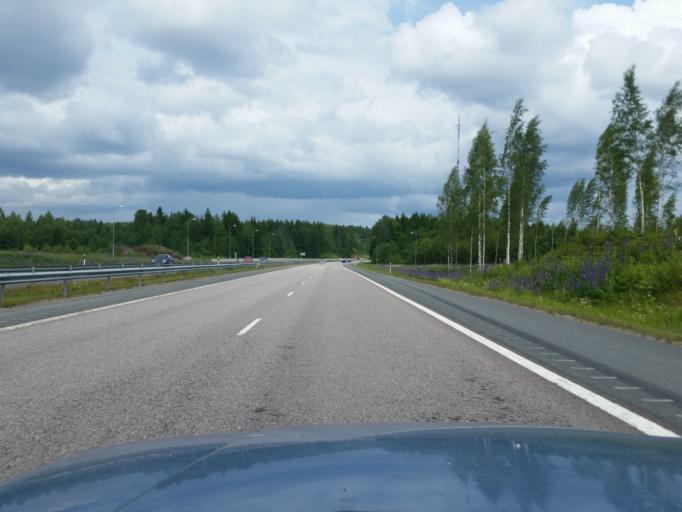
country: FI
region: Paijanne Tavastia
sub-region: Lahti
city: Lahti
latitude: 60.9980
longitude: 25.7859
